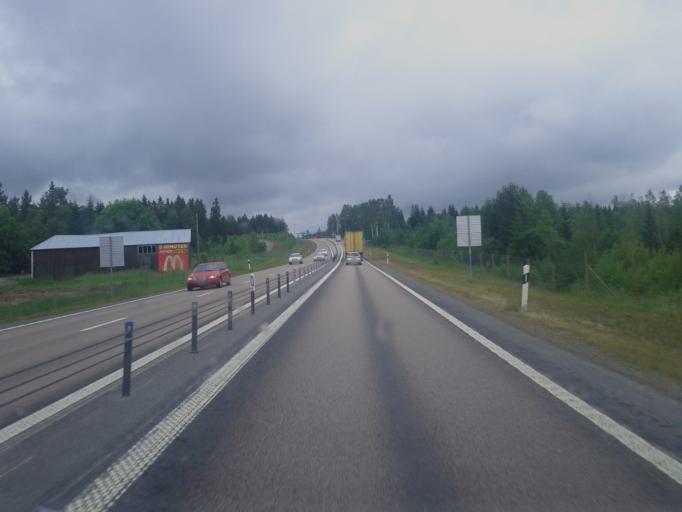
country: SE
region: Vaesternorrland
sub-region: Haernoesands Kommun
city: Haernoesand
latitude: 62.5954
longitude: 17.8027
